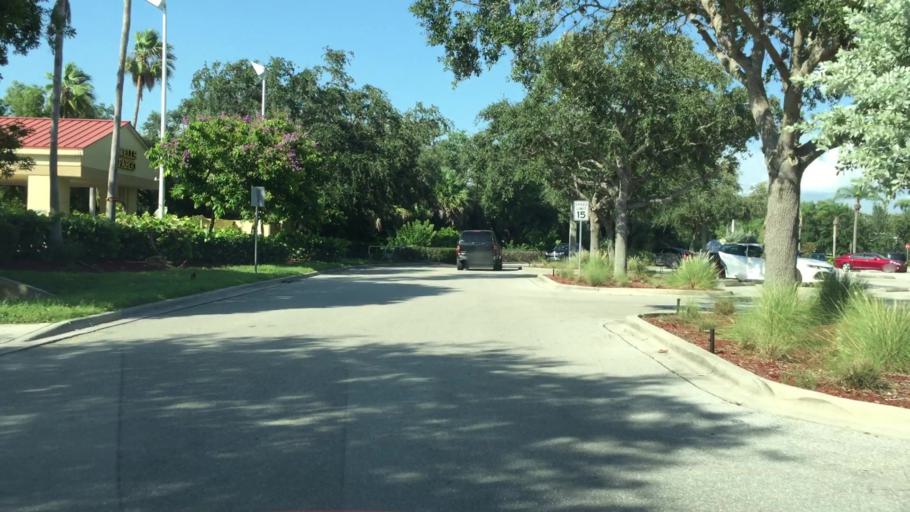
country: US
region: Florida
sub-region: Lee County
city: Estero
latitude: 26.4303
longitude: -81.8092
